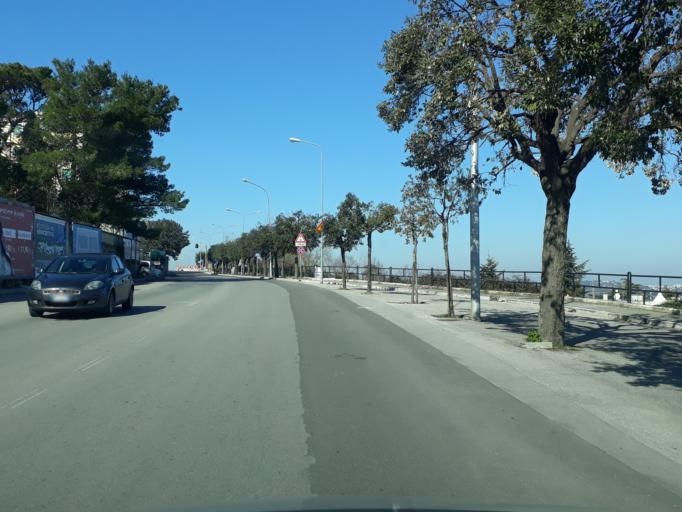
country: IT
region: Apulia
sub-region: Provincia di Taranto
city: Martina Franca
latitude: 40.7052
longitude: 17.3458
